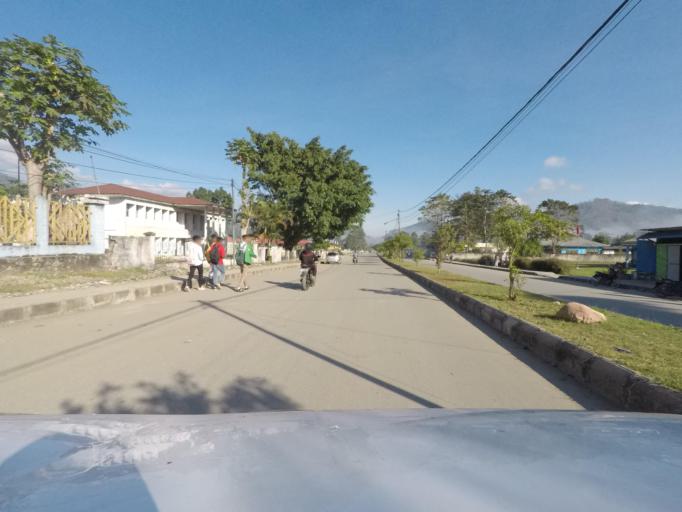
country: TL
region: Ermera
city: Gleno
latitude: -8.7239
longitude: 125.4356
